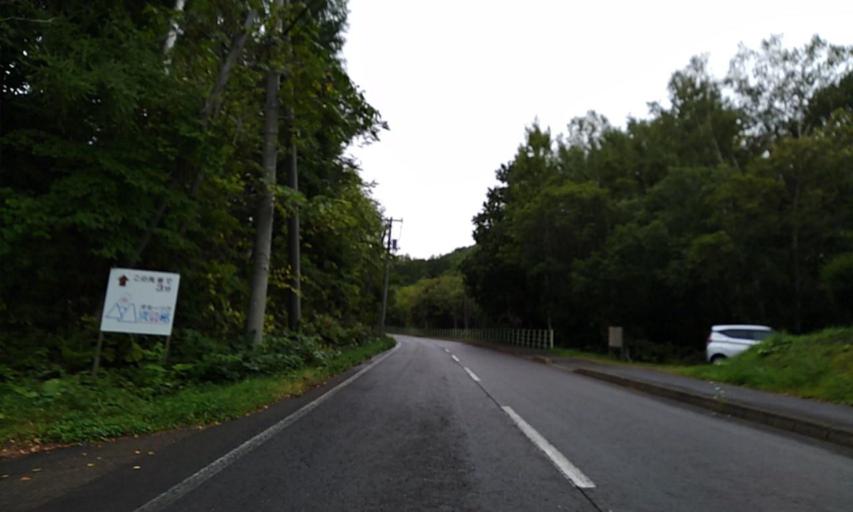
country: JP
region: Hokkaido
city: Abashiri
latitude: 44.0017
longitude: 144.2306
